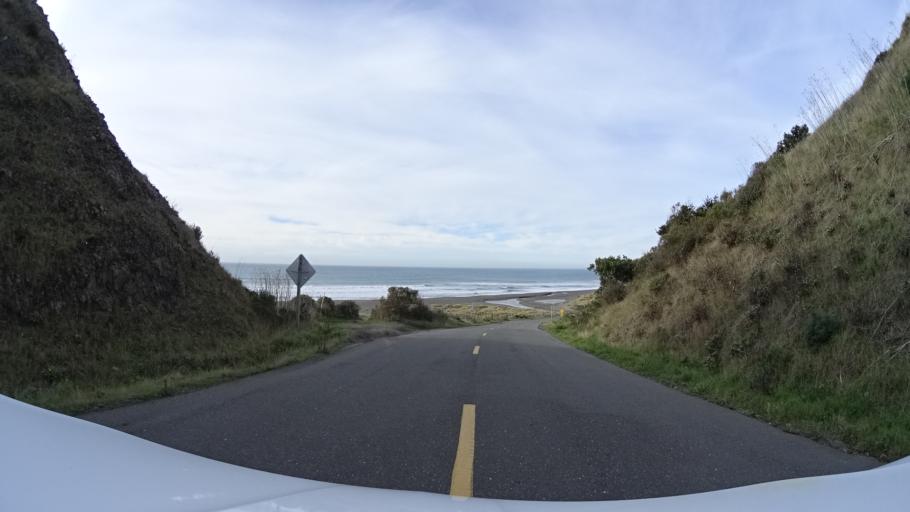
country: US
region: California
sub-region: Humboldt County
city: Ferndale
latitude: 40.3507
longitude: -124.3593
